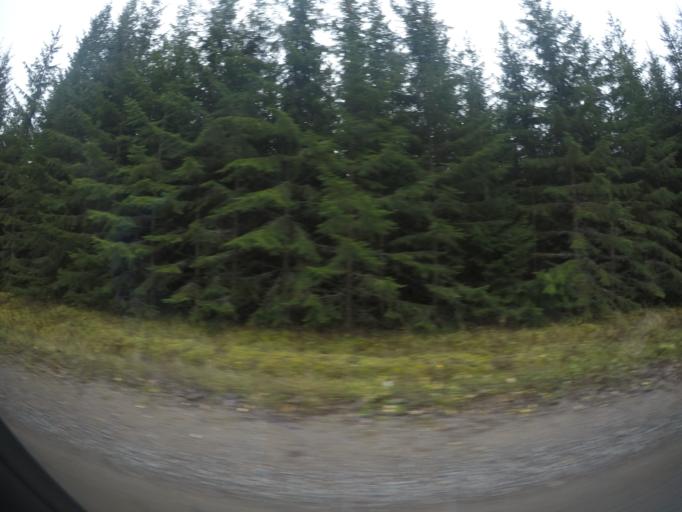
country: SE
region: Vaestmanland
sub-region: Surahammars Kommun
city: Ramnas
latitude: 59.7319
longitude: 16.1094
